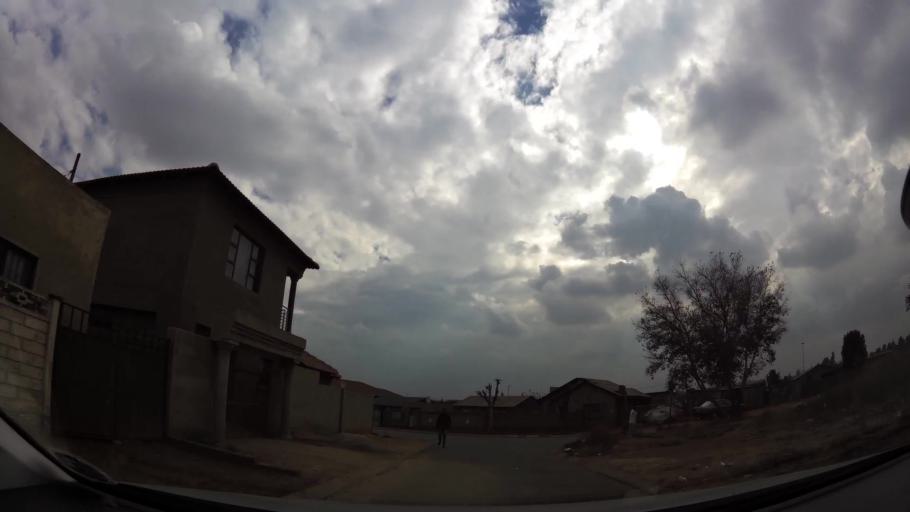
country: ZA
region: Gauteng
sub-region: City of Johannesburg Metropolitan Municipality
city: Soweto
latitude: -26.2614
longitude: 27.8518
